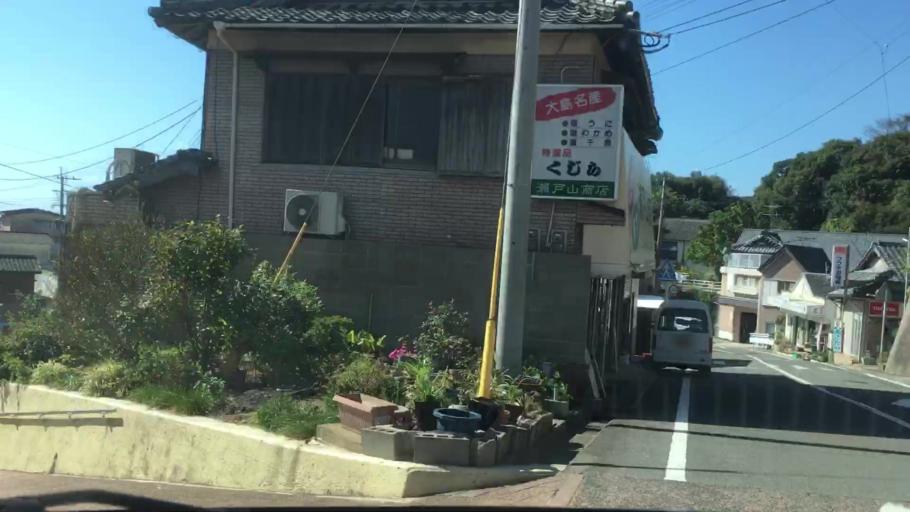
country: JP
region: Nagasaki
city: Sasebo
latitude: 33.0382
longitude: 129.6201
